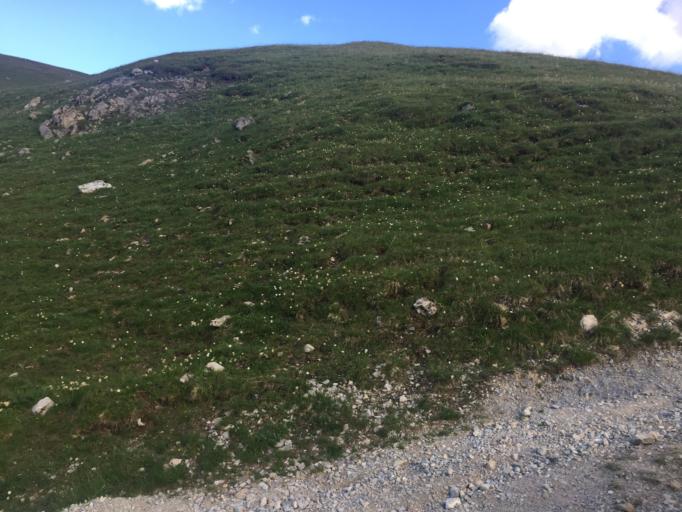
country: FR
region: Rhone-Alpes
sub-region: Departement de la Savoie
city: Modane
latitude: 45.1340
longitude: 6.6193
